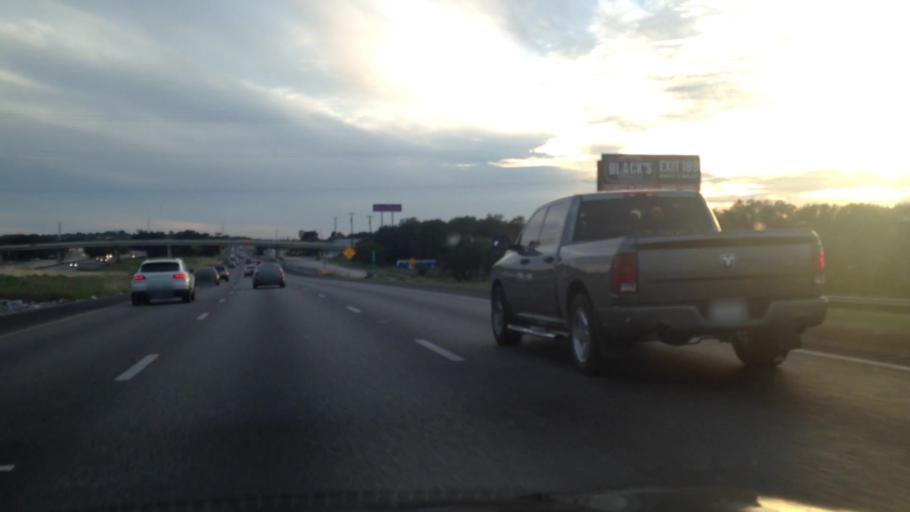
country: US
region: Texas
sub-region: Guadalupe County
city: Redwood
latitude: 29.7970
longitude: -98.0203
